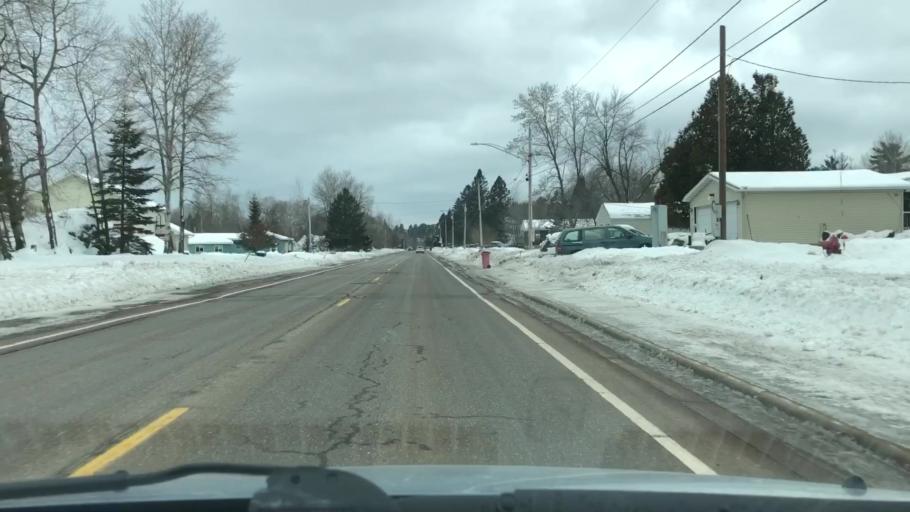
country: US
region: Minnesota
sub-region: Carlton County
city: Carlton
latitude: 46.6636
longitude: -92.3893
